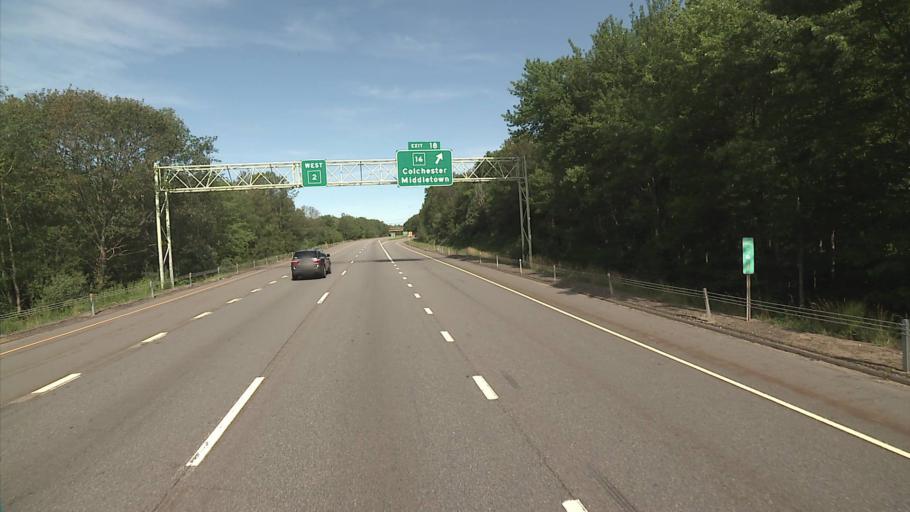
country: US
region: Connecticut
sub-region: New London County
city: Colchester
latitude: 41.5681
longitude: -72.3335
